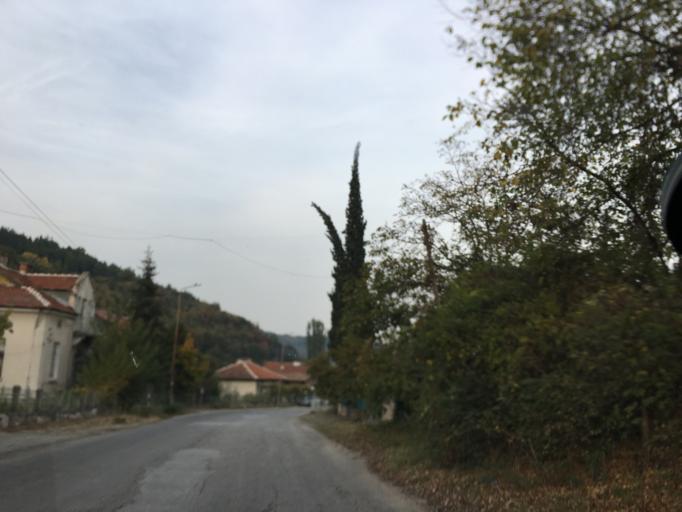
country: BG
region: Pazardzhik
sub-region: Obshtina Belovo
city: Belovo
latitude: 42.2099
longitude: 24.0093
